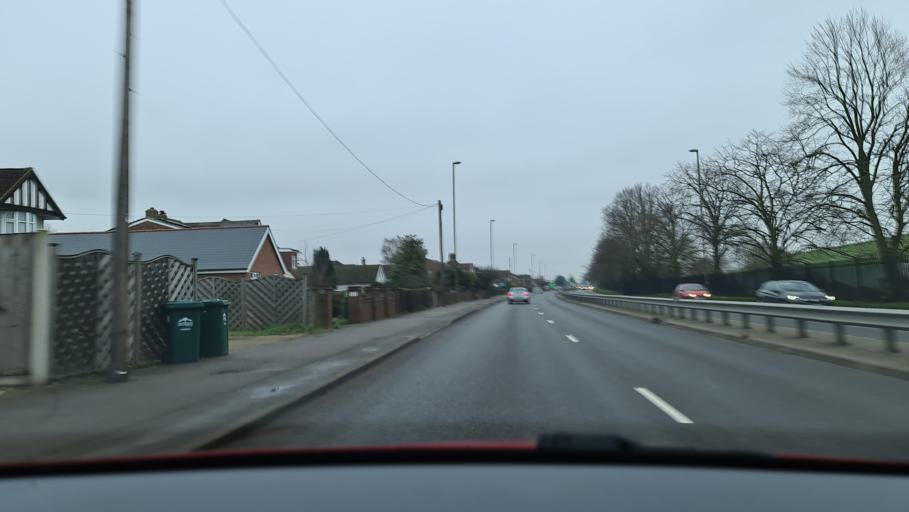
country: GB
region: England
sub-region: Surrey
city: Shepperton
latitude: 51.4238
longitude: -0.4549
